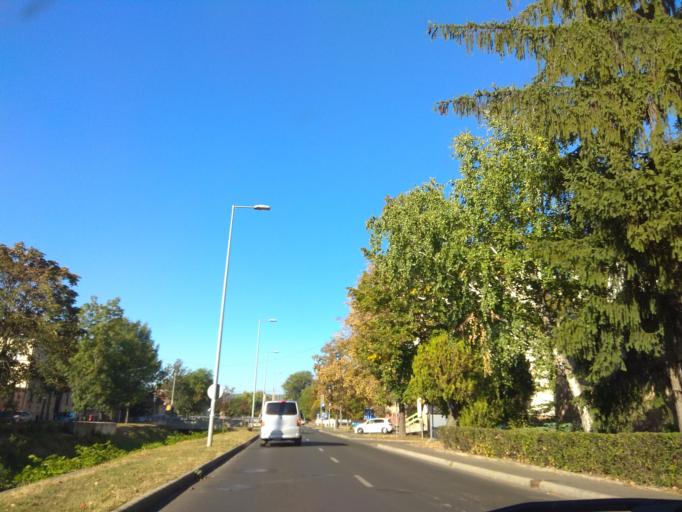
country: HU
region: Borsod-Abauj-Zemplen
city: Miskolc
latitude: 48.1028
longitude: 20.7718
